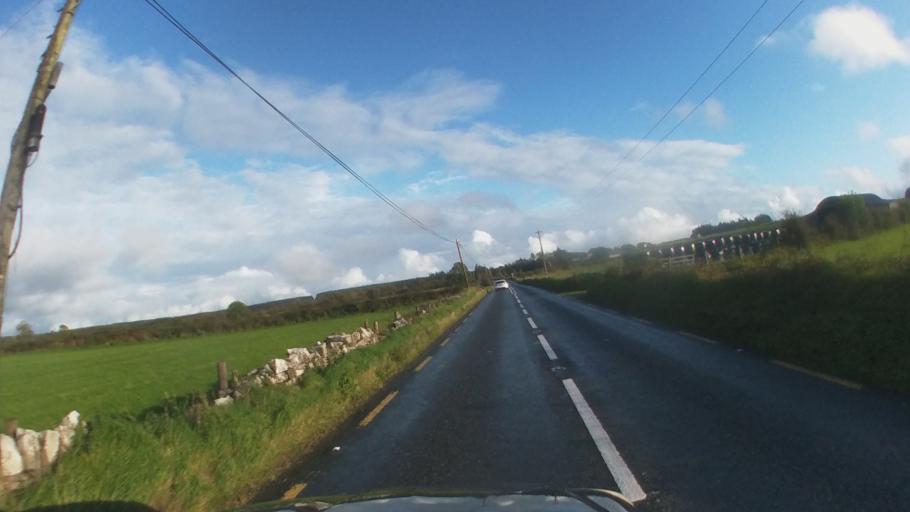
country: IE
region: Connaught
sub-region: Roscommon
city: Castlerea
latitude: 53.8277
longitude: -8.3634
